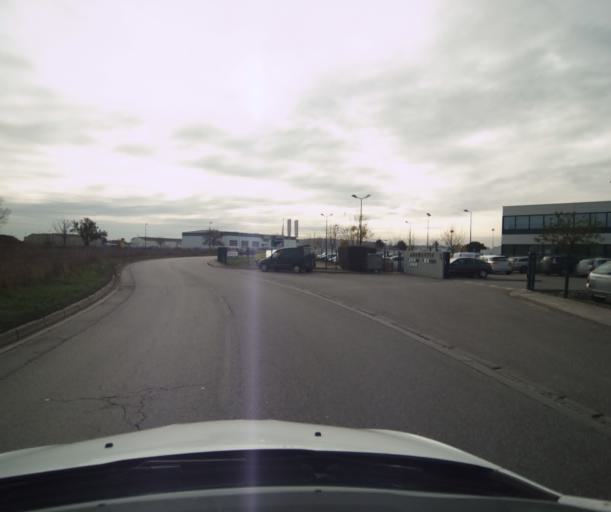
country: FR
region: Midi-Pyrenees
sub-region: Departement de la Haute-Garonne
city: Lespinasse
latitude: 43.7191
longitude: 1.3958
